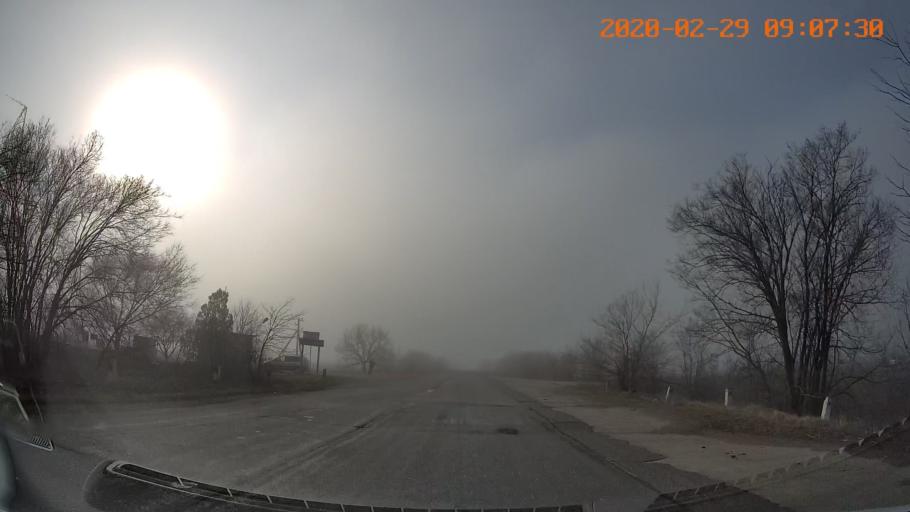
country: MD
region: Telenesti
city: Tiraspolul Nou
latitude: 46.8613
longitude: 29.7491
